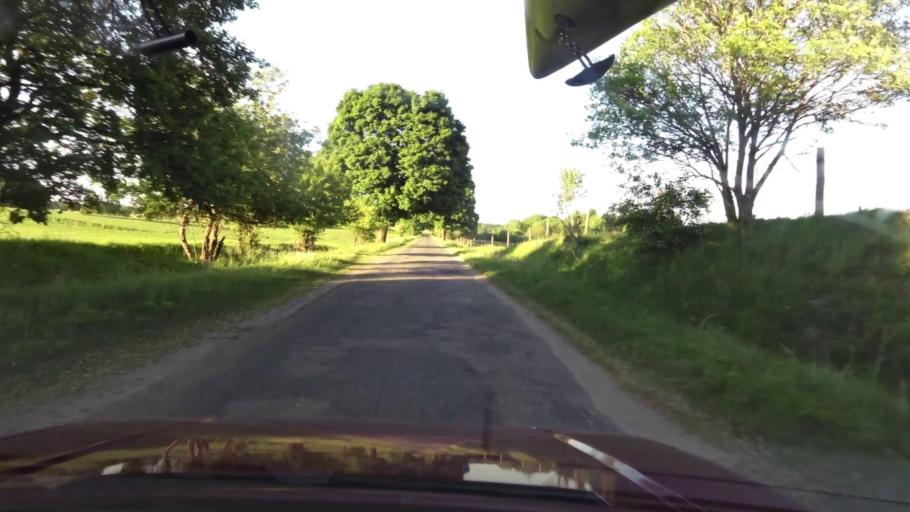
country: PL
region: West Pomeranian Voivodeship
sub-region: Powiat szczecinecki
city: Bialy Bor
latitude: 53.9433
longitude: 16.7663
